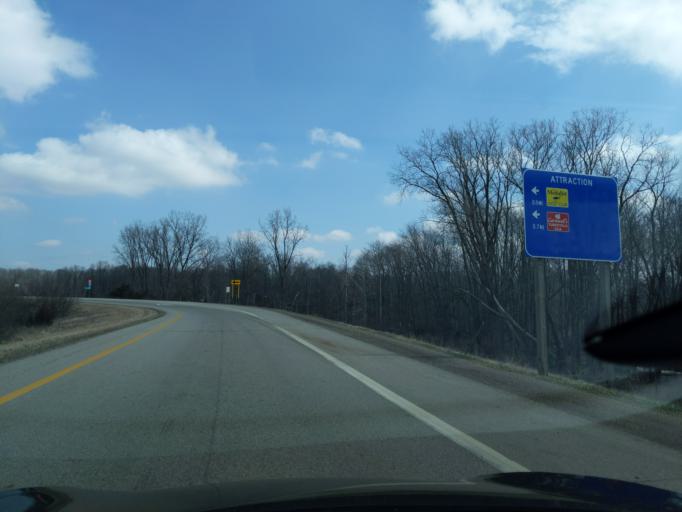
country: US
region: Michigan
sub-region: Calhoun County
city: Marshall
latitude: 42.3482
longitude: -84.9794
